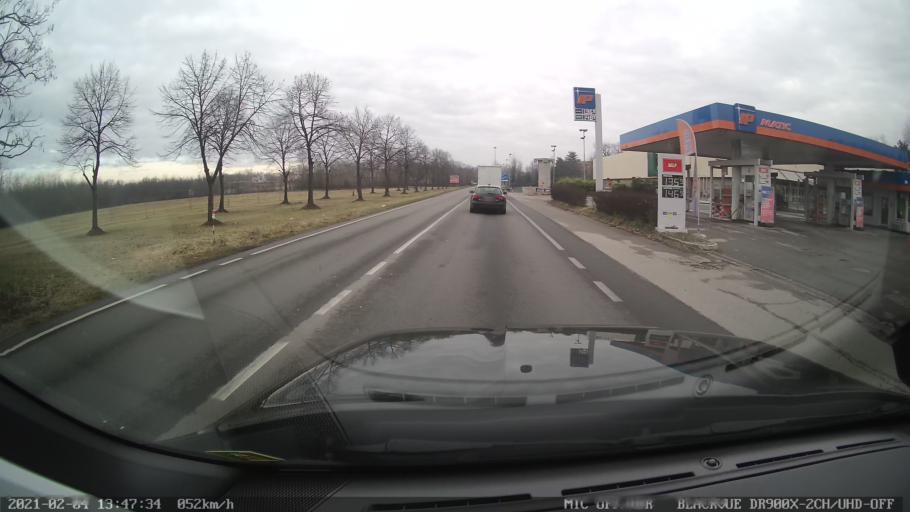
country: IT
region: Lombardy
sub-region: Provincia di Varese
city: Solbiate Olona
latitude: 45.6457
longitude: 8.8648
